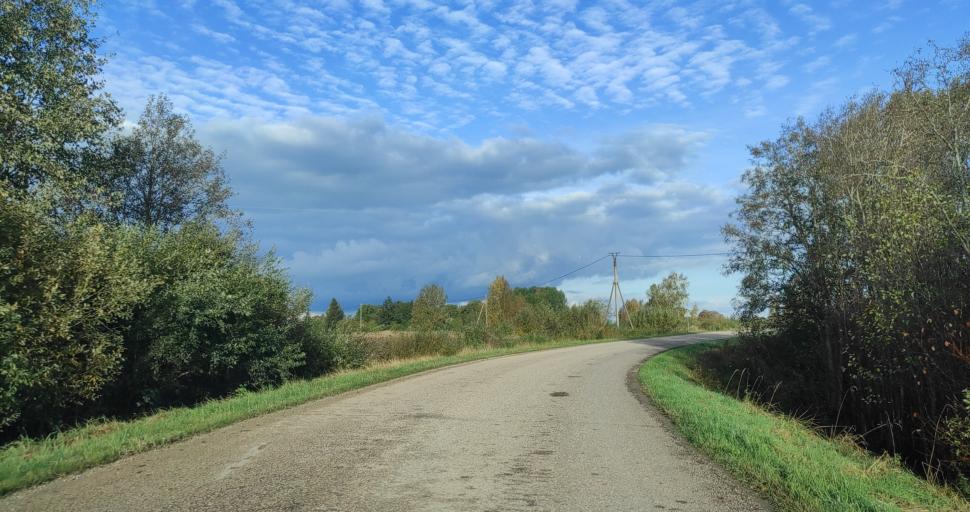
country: LV
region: Aizpute
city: Aizpute
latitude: 56.7515
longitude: 21.7847
